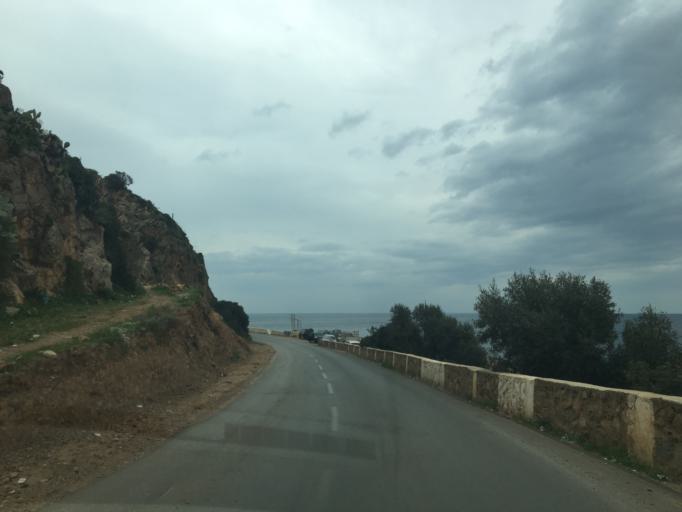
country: DZ
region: Tipaza
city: Tipasa
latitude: 36.6227
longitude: 2.4076
